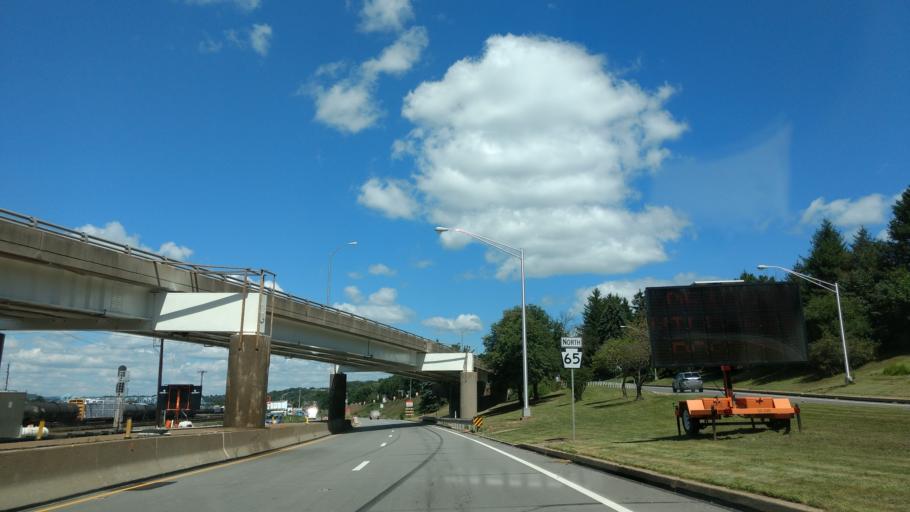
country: US
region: Pennsylvania
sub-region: Beaver County
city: Freedom
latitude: 40.6801
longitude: -80.2497
